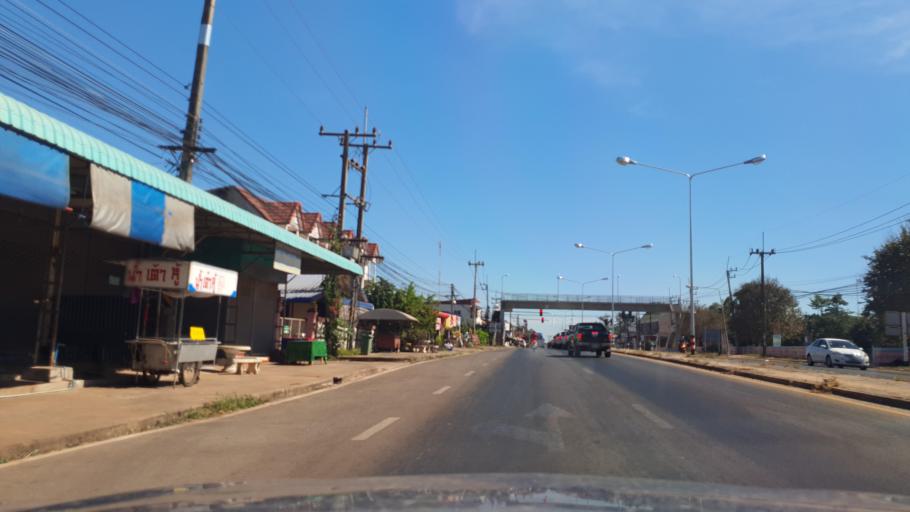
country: TH
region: Sakon Nakhon
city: Sakon Nakhon
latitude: 17.0838
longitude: 104.1895
